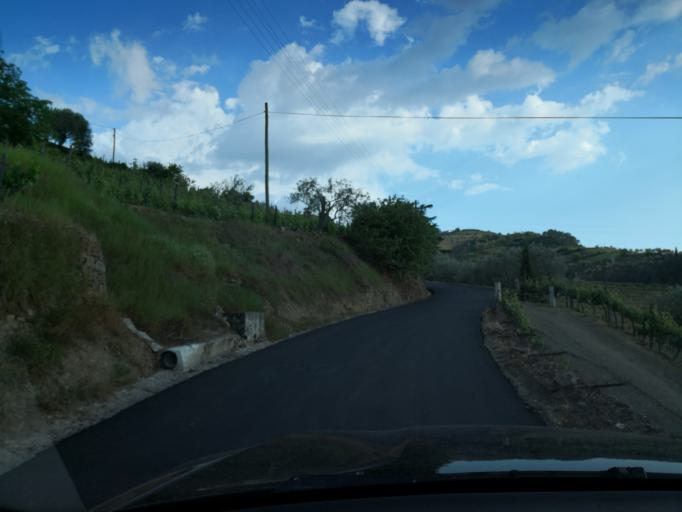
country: PT
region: Vila Real
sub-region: Santa Marta de Penaguiao
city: Santa Marta de Penaguiao
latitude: 41.2198
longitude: -7.7178
